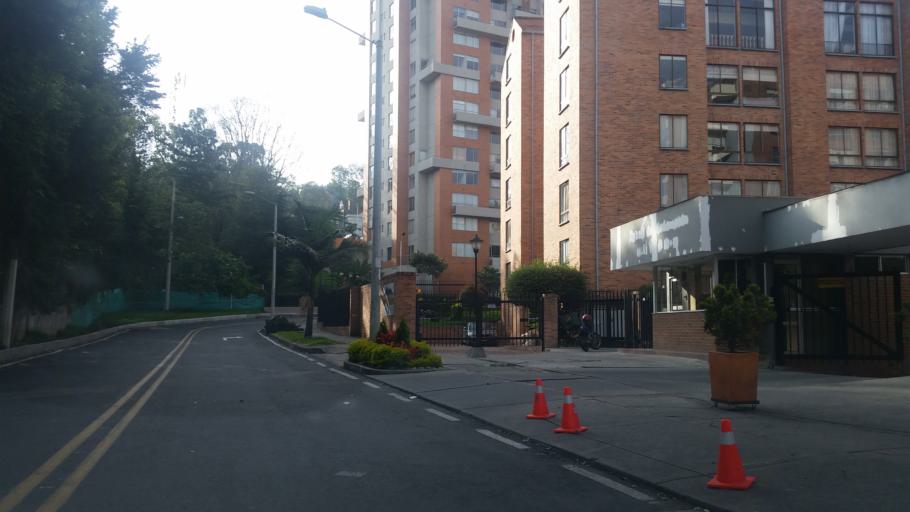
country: CO
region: Cundinamarca
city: Cota
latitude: 4.7513
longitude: -74.0674
